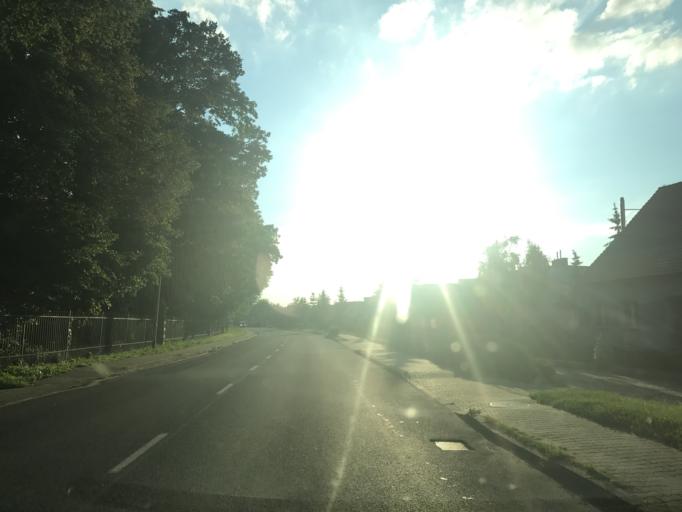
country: PL
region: Greater Poland Voivodeship
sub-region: Powiat jarocinski
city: Jaraczewo
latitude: 51.9770
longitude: 17.3664
